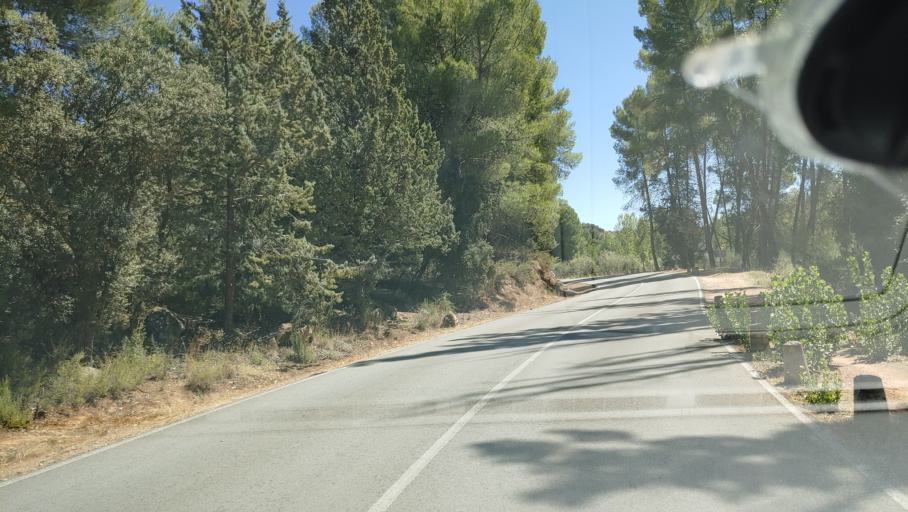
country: ES
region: Castille-La Mancha
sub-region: Provincia de Ciudad Real
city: Ruidera
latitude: 38.9625
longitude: -2.8753
